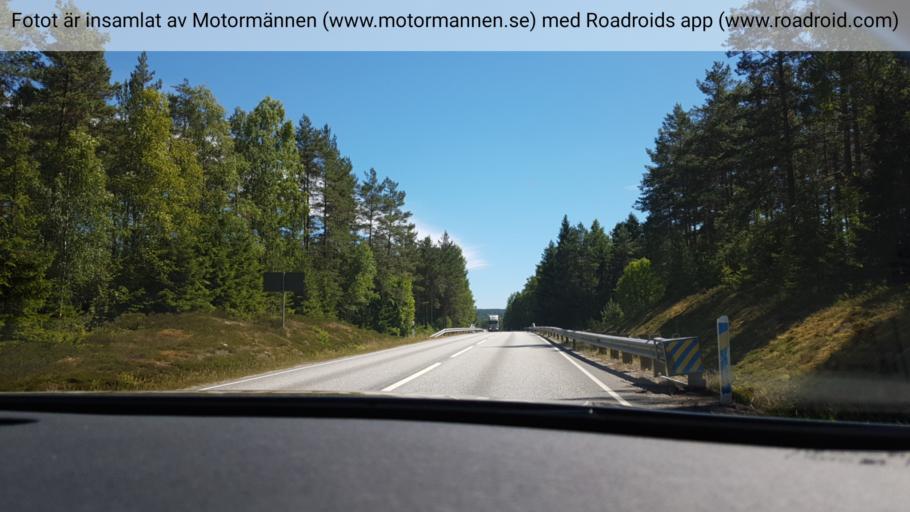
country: SE
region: Joenkoeping
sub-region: Gnosjo Kommun
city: Gnosjoe
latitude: 57.3667
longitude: 13.7447
